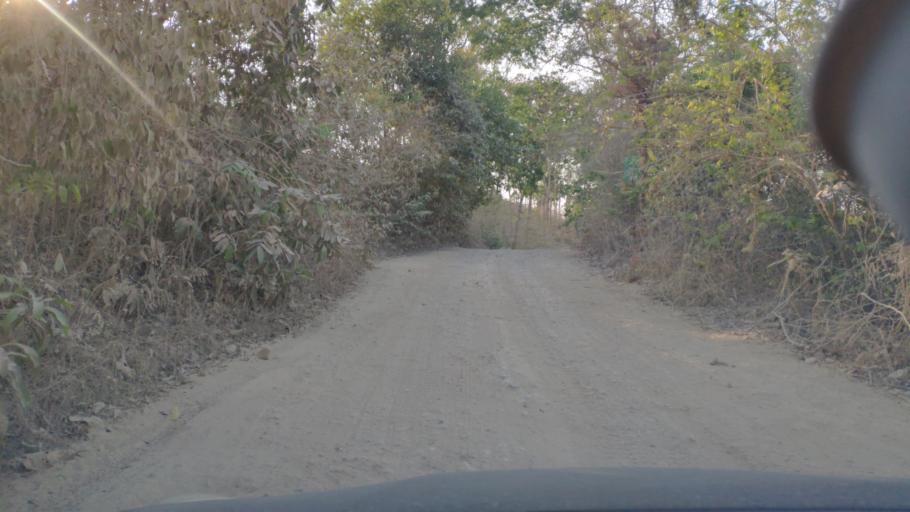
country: ID
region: Central Java
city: Sendangrejo
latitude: -6.9100
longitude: 111.5529
